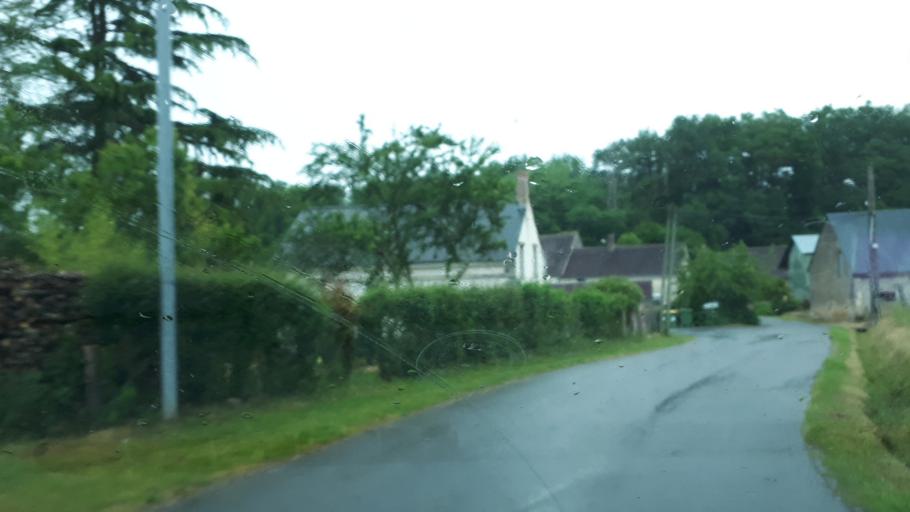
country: FR
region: Centre
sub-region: Departement du Loir-et-Cher
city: Lunay
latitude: 47.7918
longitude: 0.8888
